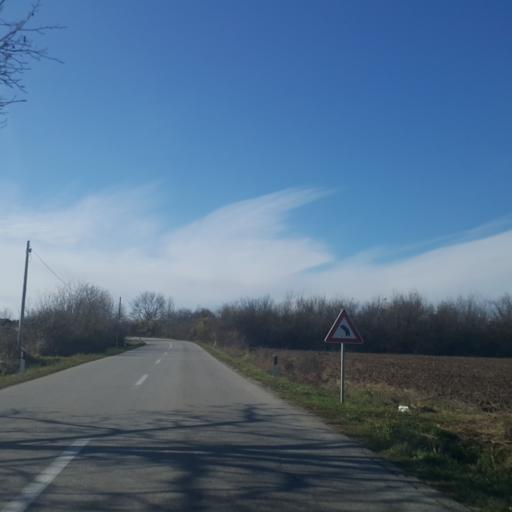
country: RS
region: Central Serbia
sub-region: Sumadijski Okrug
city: Topola
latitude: 44.2516
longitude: 20.7886
